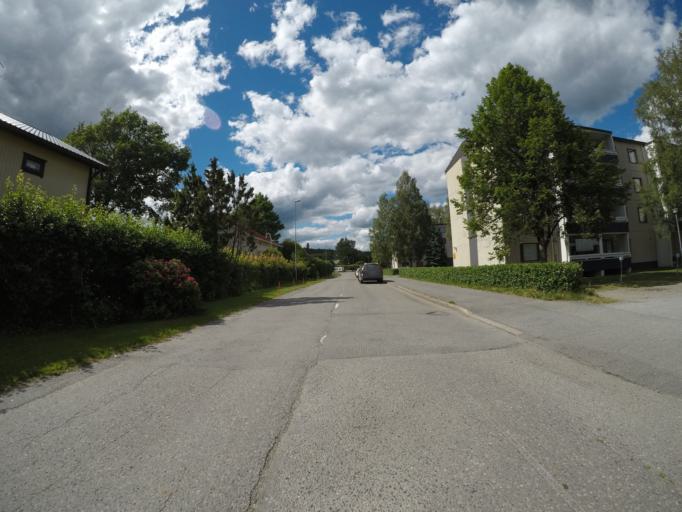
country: FI
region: Haeme
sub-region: Haemeenlinna
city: Haemeenlinna
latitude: 60.9975
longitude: 24.4349
